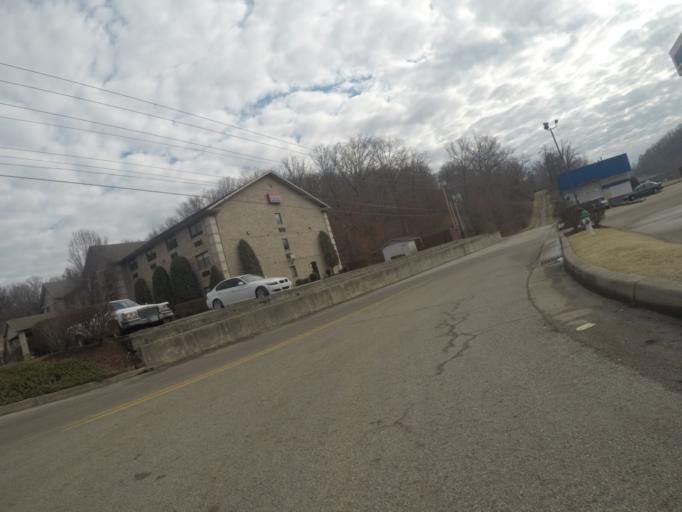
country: US
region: West Virginia
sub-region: Cabell County
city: Huntington
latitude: 38.3960
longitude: -82.4124
